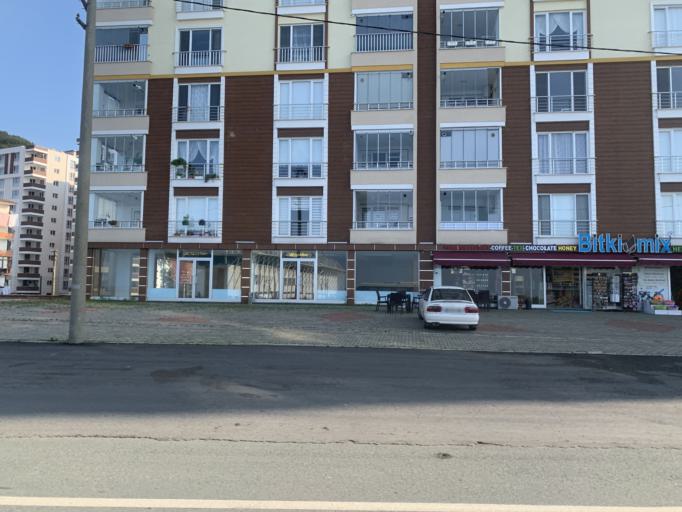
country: TR
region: Trabzon
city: Of
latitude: 40.9386
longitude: 40.2542
